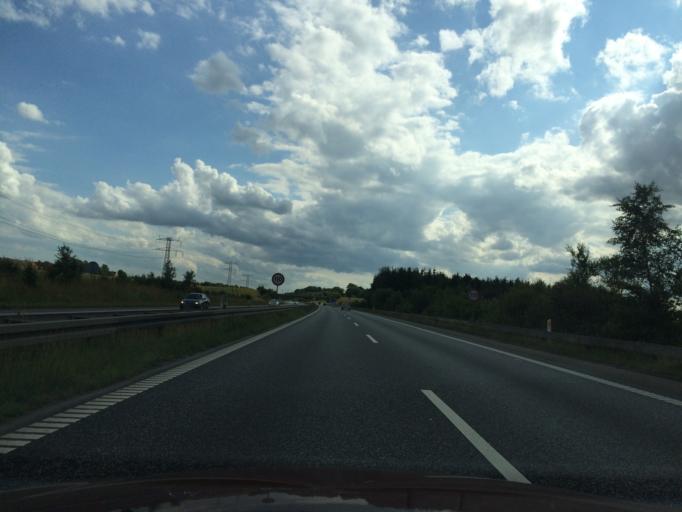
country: DK
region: Central Jutland
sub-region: Favrskov Kommune
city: Soften
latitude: 56.2001
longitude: 10.0766
